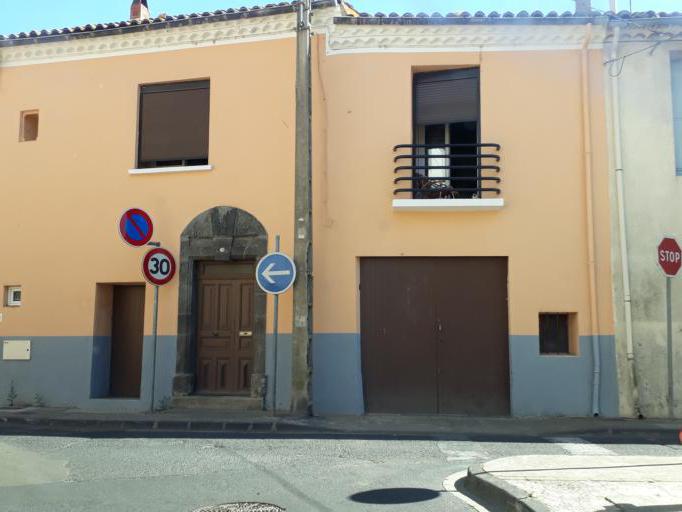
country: FR
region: Languedoc-Roussillon
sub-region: Departement de l'Herault
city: Agde
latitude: 43.3141
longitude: 3.4733
